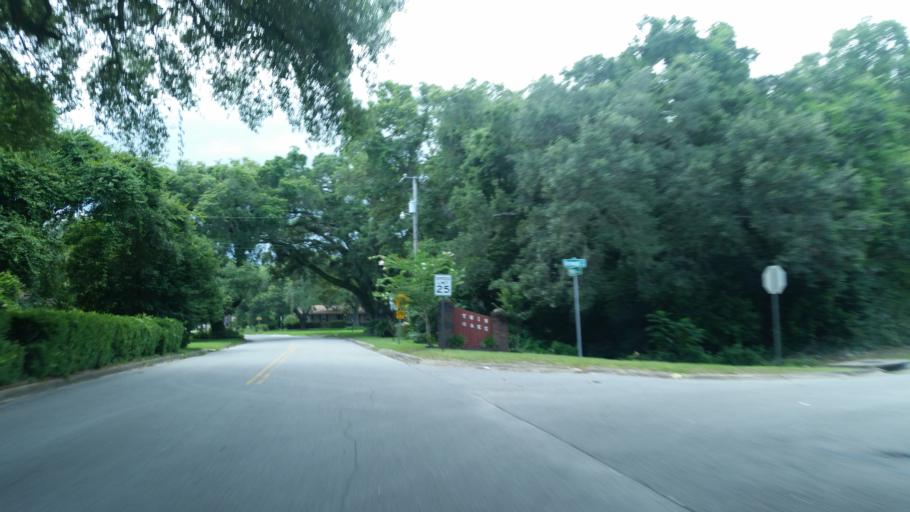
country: US
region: Florida
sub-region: Escambia County
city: West Pensacola
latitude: 30.4104
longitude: -87.2821
